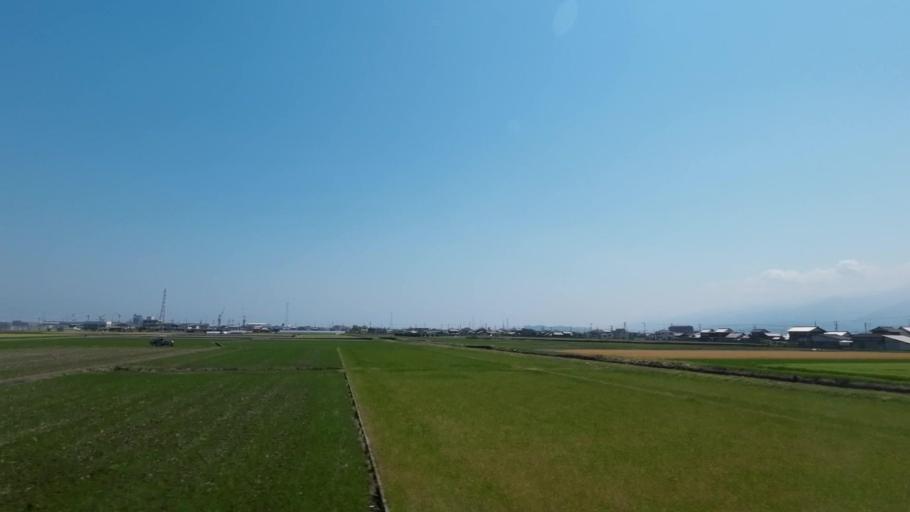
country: JP
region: Ehime
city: Saijo
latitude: 33.9151
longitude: 133.0984
